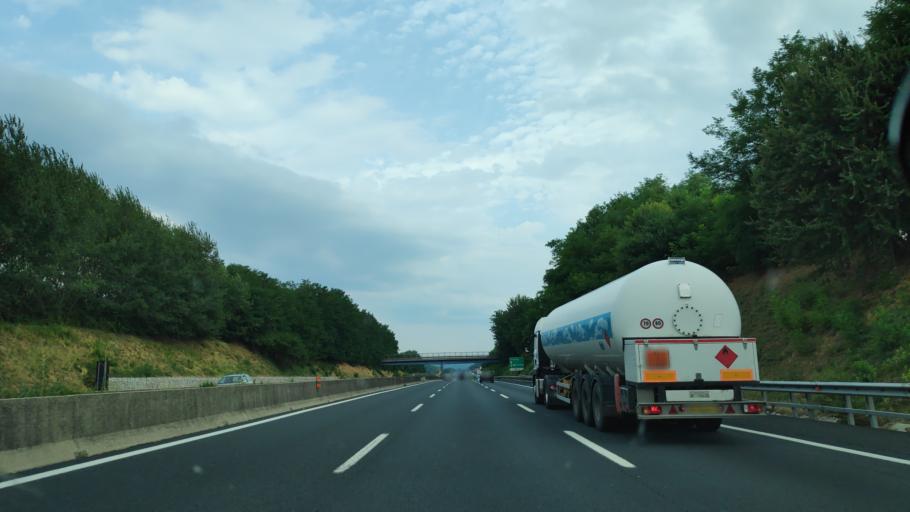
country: IT
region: Latium
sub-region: Provincia di Frosinone
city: Frosinone
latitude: 41.6244
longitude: 13.2984
